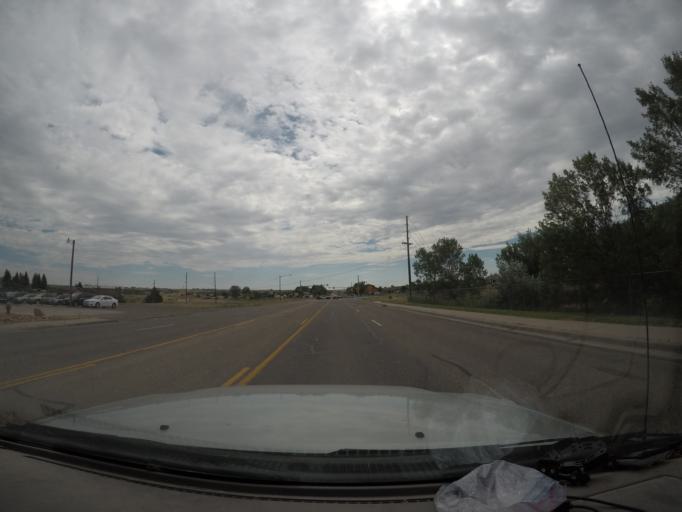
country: US
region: Wyoming
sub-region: Laramie County
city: Fox Farm-College
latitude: 41.1455
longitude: -104.7578
